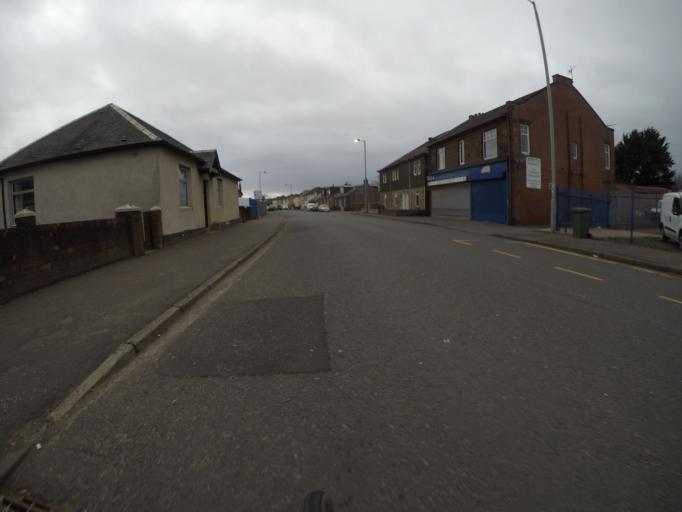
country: GB
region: Scotland
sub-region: East Ayrshire
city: Crosshouse
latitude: 55.6124
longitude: -4.5536
